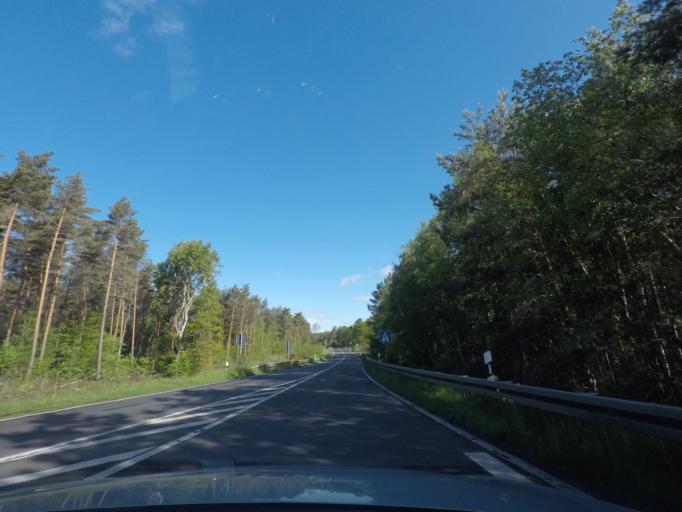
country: DE
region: Saxony-Anhalt
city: Harbke
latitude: 52.2182
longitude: 11.0524
